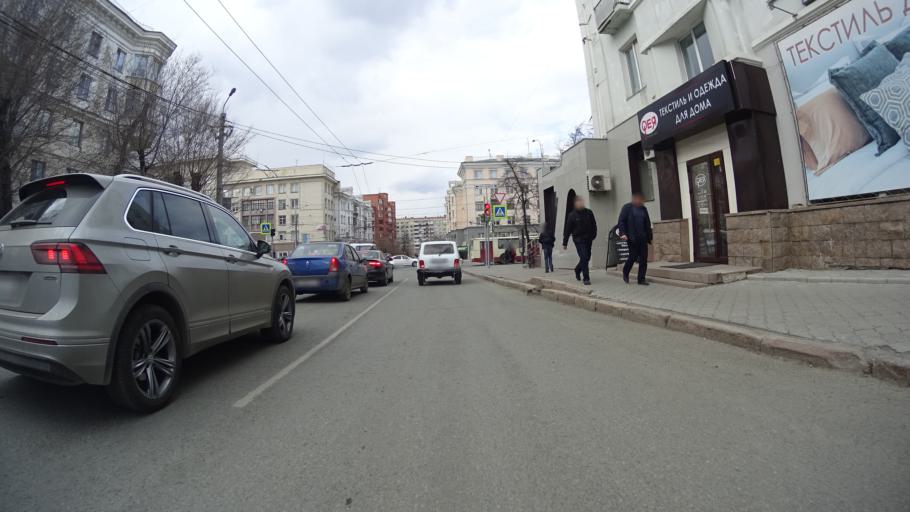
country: RU
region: Chelyabinsk
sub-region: Gorod Chelyabinsk
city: Chelyabinsk
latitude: 55.1600
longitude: 61.4090
